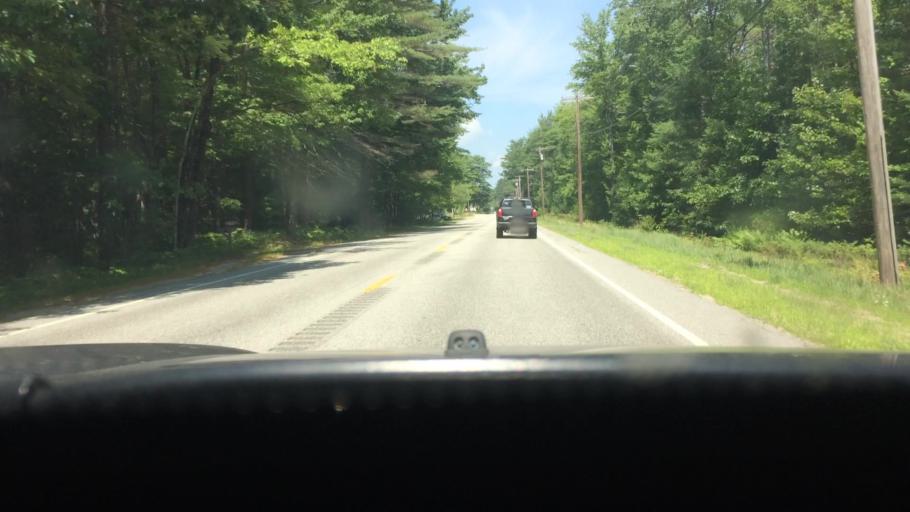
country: US
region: Maine
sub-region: Androscoggin County
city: Mechanic Falls
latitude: 44.0986
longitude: -70.3600
